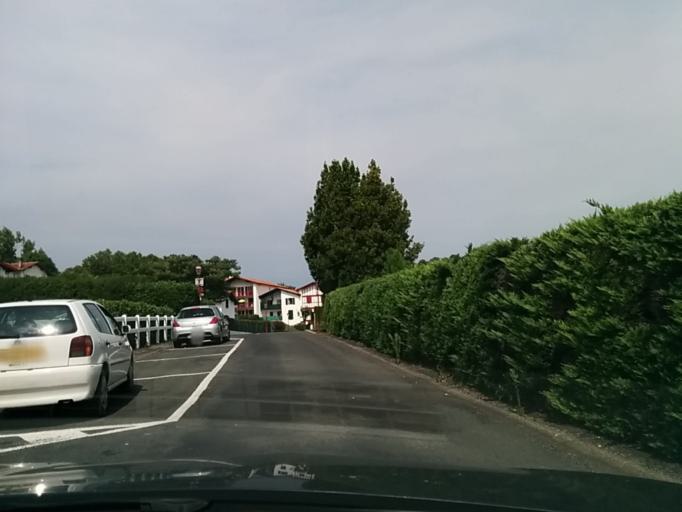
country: FR
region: Aquitaine
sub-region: Departement des Pyrenees-Atlantiques
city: Urrugne
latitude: 43.3640
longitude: -1.7006
